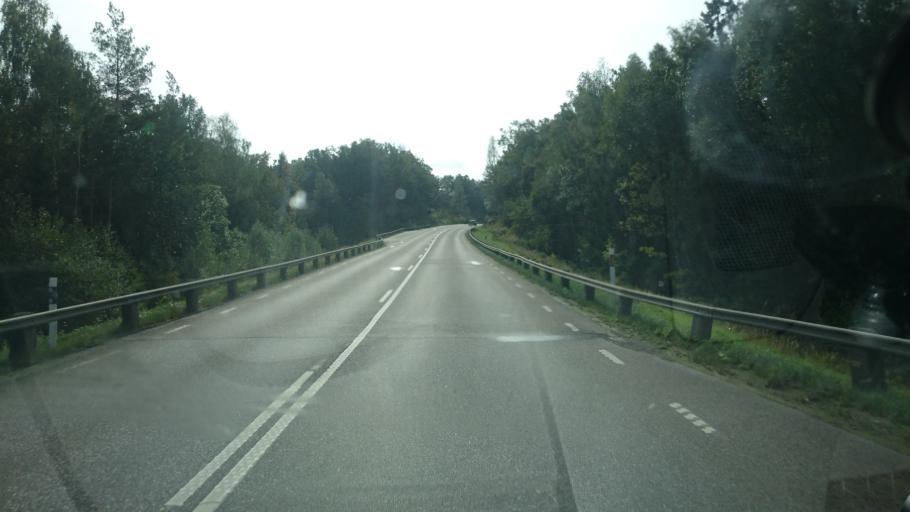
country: SE
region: Vaestra Goetaland
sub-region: Alingsas Kommun
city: Sollebrunn
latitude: 58.0524
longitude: 12.4675
